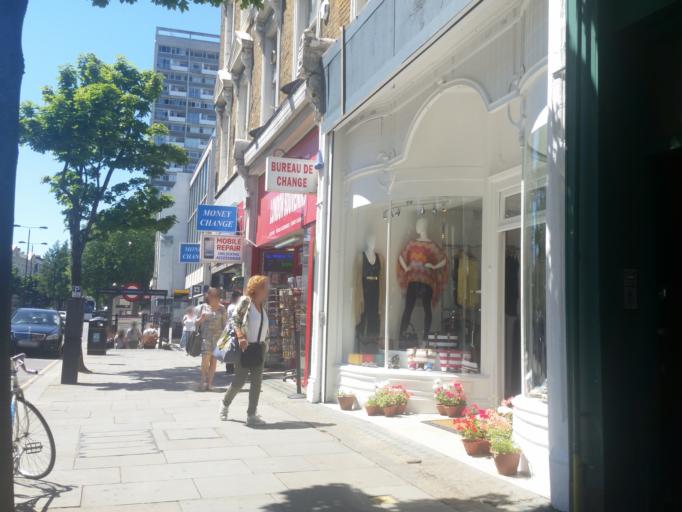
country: GB
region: England
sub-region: Greater London
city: Kensington
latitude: 51.5092
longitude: -0.1957
